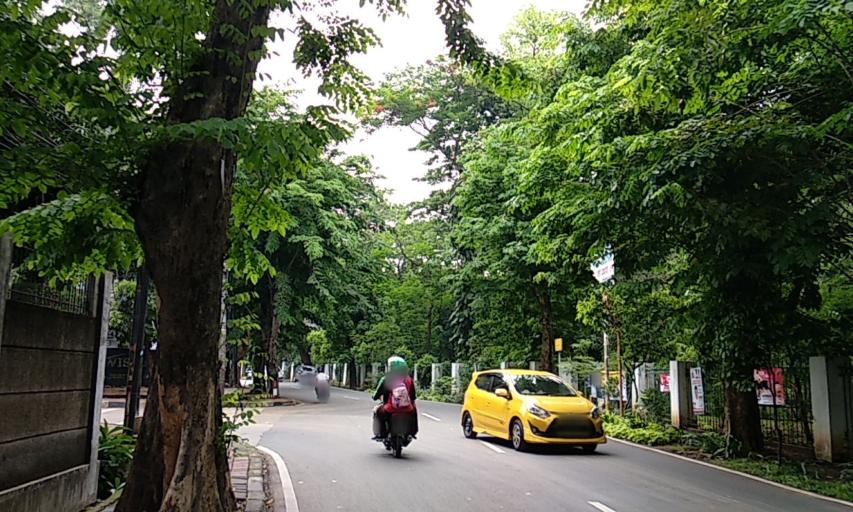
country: ID
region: Jakarta Raya
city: Jakarta
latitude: -6.2403
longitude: 106.8530
